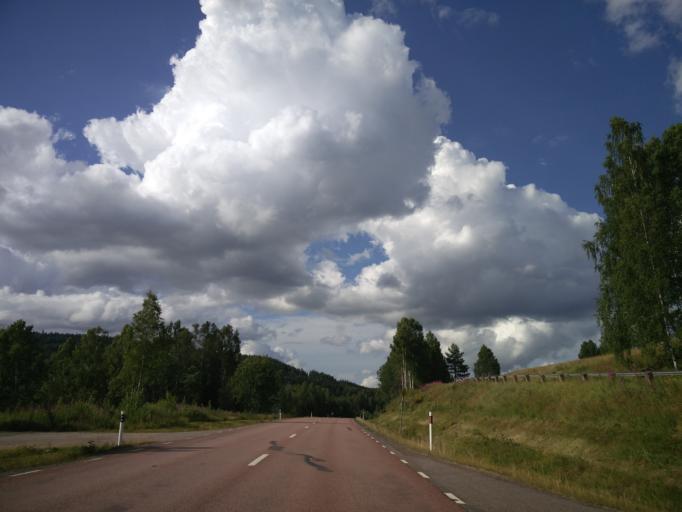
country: SE
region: Vaermland
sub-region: Torsby Kommun
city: Torsby
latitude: 60.2405
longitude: 13.0094
